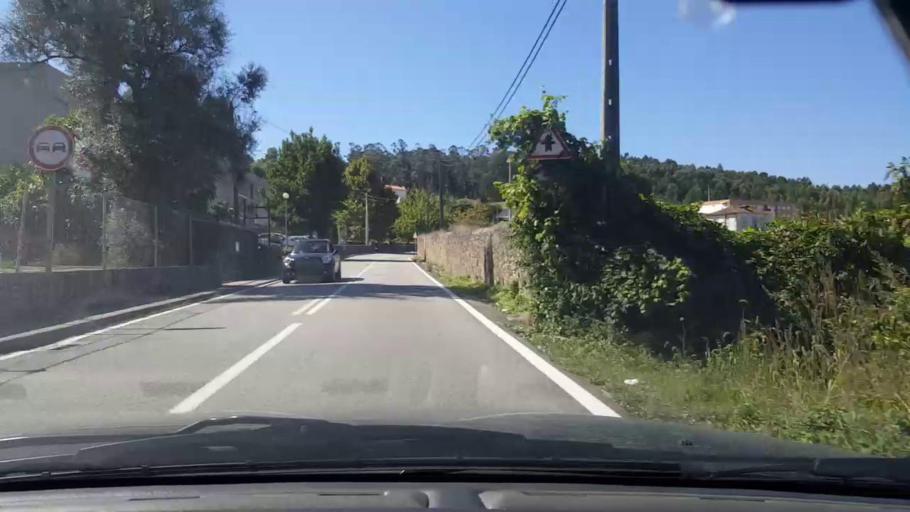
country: PT
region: Porto
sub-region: Maia
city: Gemunde
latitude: 41.3387
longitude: -8.6430
